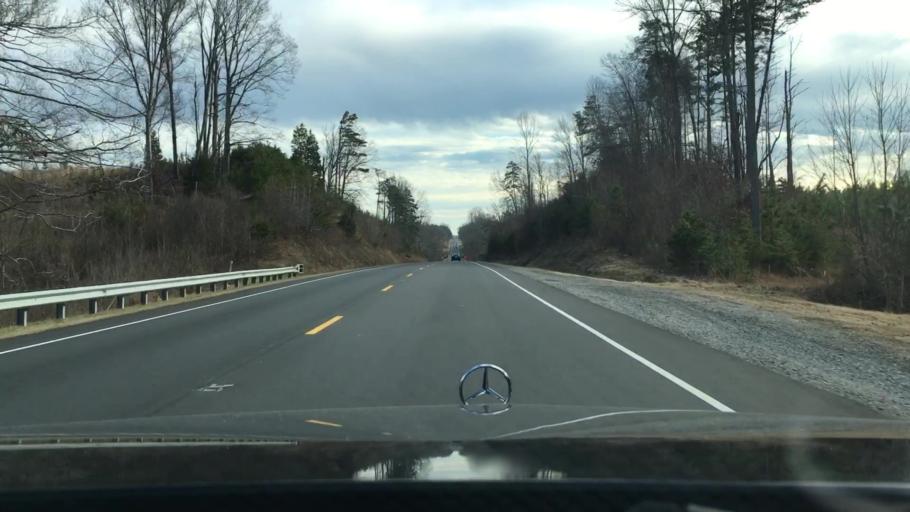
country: US
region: Virginia
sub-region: City of Danville
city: Danville
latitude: 36.5105
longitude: -79.3910
